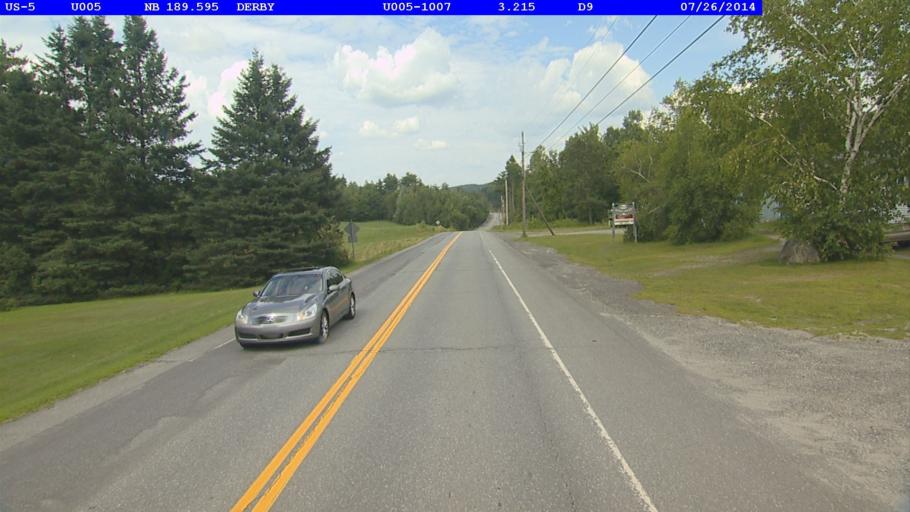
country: US
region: Vermont
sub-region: Orleans County
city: Newport
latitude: 44.9704
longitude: -72.1204
